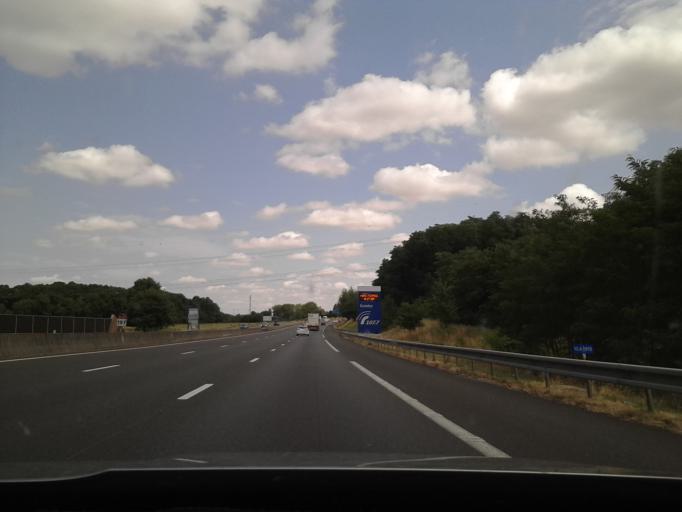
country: FR
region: Centre
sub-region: Departement d'Indre-et-Loire
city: Parcay-Meslay
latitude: 47.4687
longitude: 0.7678
